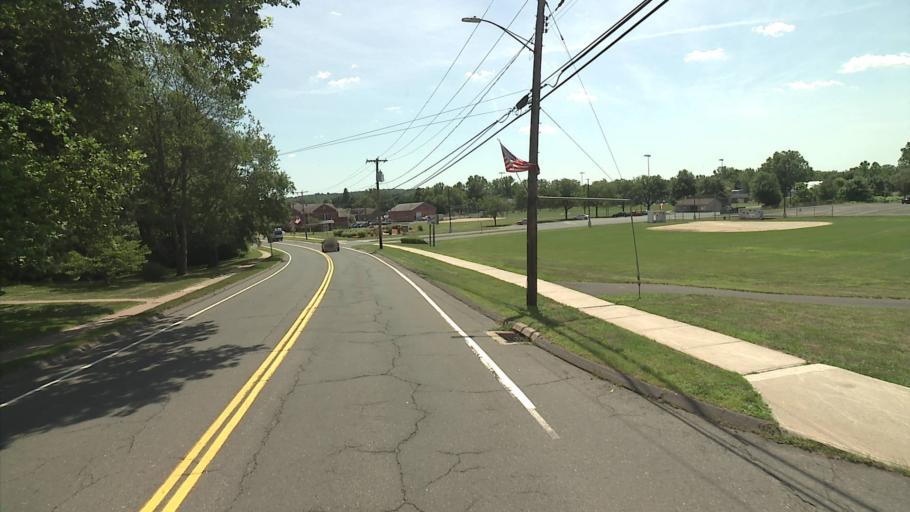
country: US
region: Connecticut
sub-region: Middlesex County
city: Cromwell
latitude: 41.5967
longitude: -72.6487
